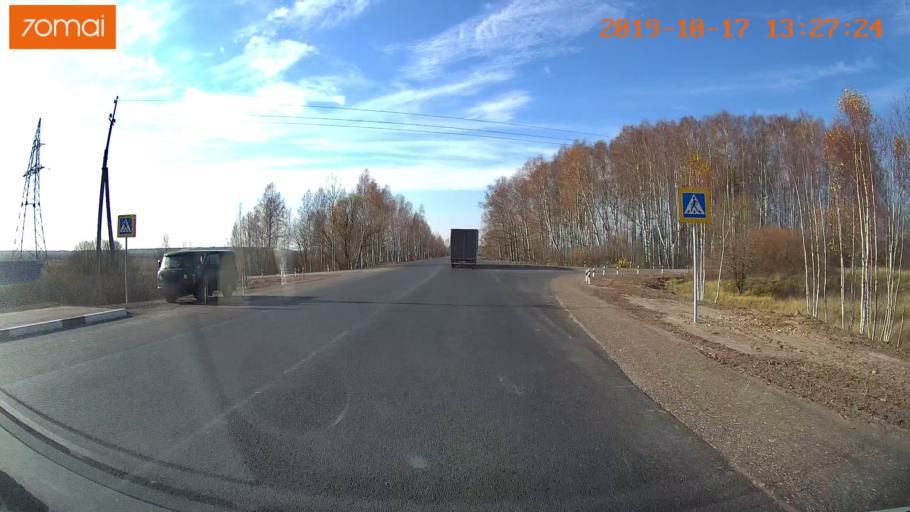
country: RU
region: Vladimir
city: Velikodvorskiy
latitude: 55.1131
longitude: 40.8960
